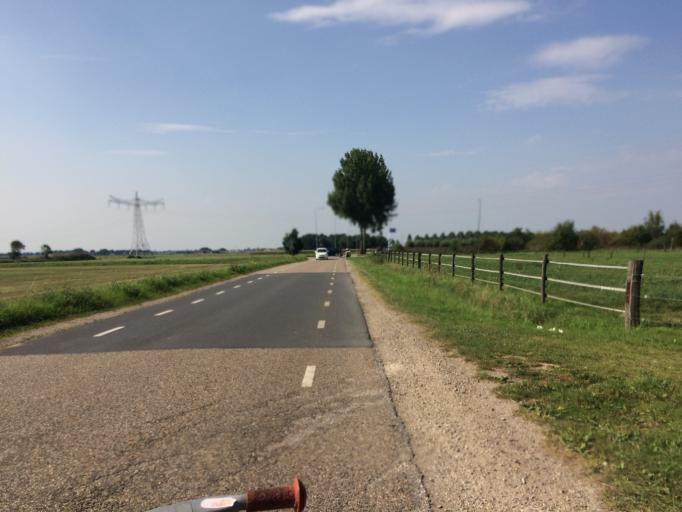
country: NL
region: Gelderland
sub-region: Gemeente Maasdriel
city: Hedel
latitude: 51.7194
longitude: 5.2445
